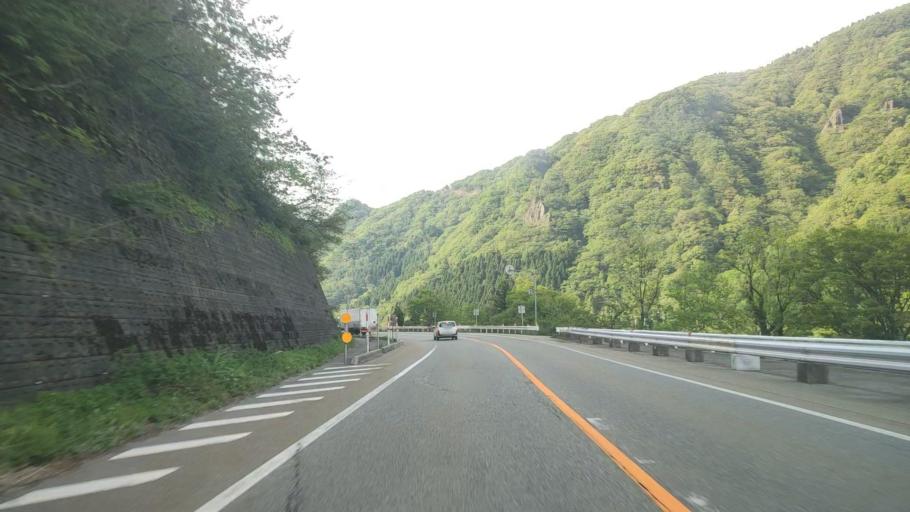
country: JP
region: Toyama
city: Yatsuomachi-higashikumisaka
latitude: 36.5414
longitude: 137.2295
